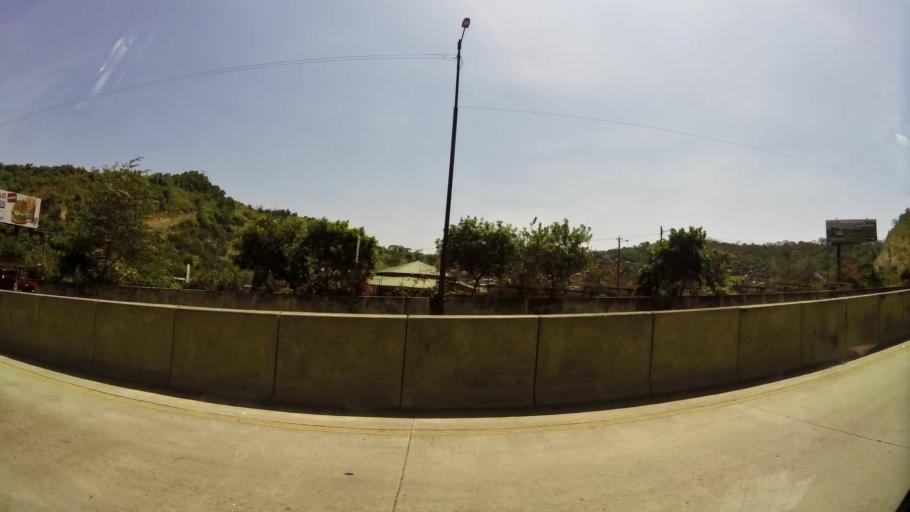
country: EC
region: Guayas
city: Guayaquil
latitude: -2.1818
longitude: -79.9290
